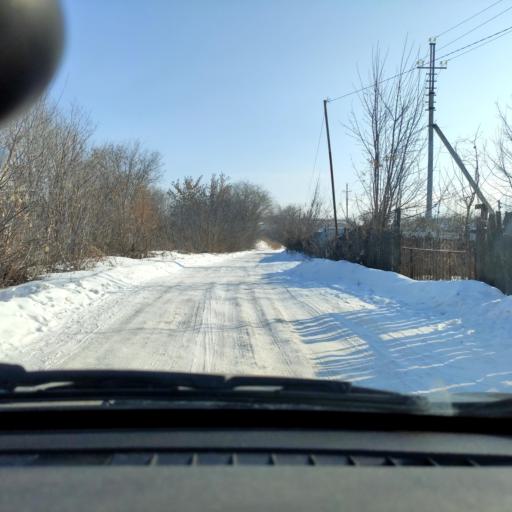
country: RU
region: Samara
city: Tol'yatti
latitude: 53.5703
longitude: 49.4545
